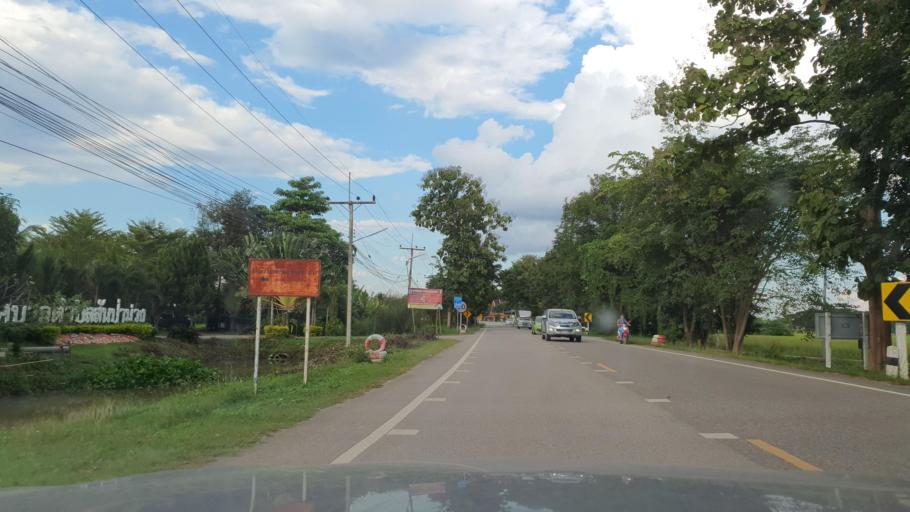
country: TH
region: Phayao
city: Phayao
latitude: 19.1763
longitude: 99.8347
